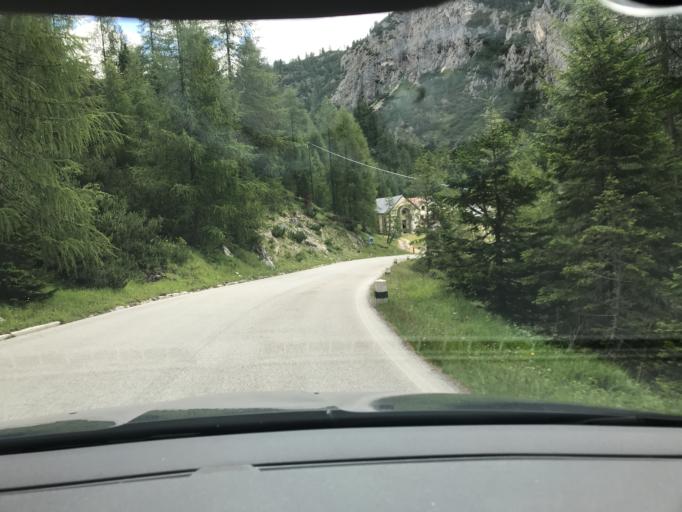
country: IT
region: Veneto
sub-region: Provincia di Belluno
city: Livinallongo del Col di Lana
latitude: 46.5143
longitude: 12.0005
